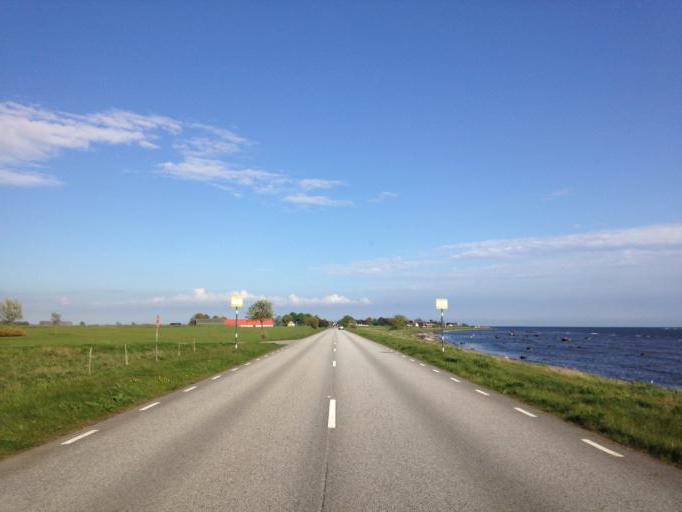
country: SE
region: Skane
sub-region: Trelleborgs Kommun
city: Skare
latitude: 55.3807
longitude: 13.0367
